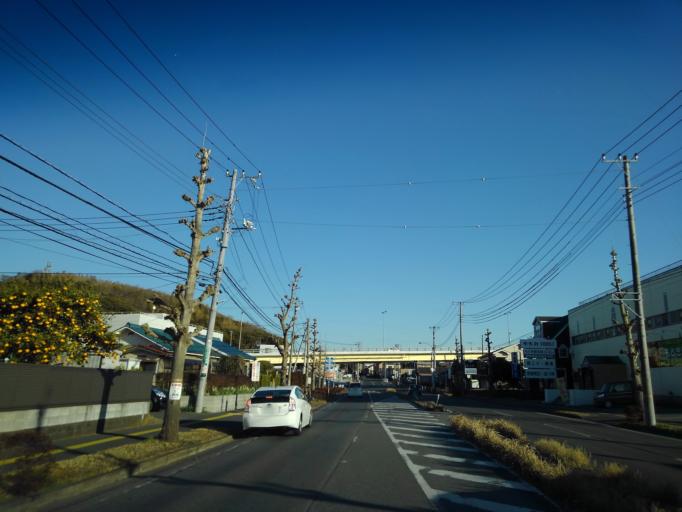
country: JP
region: Chiba
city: Kimitsu
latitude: 35.3327
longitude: 139.9021
